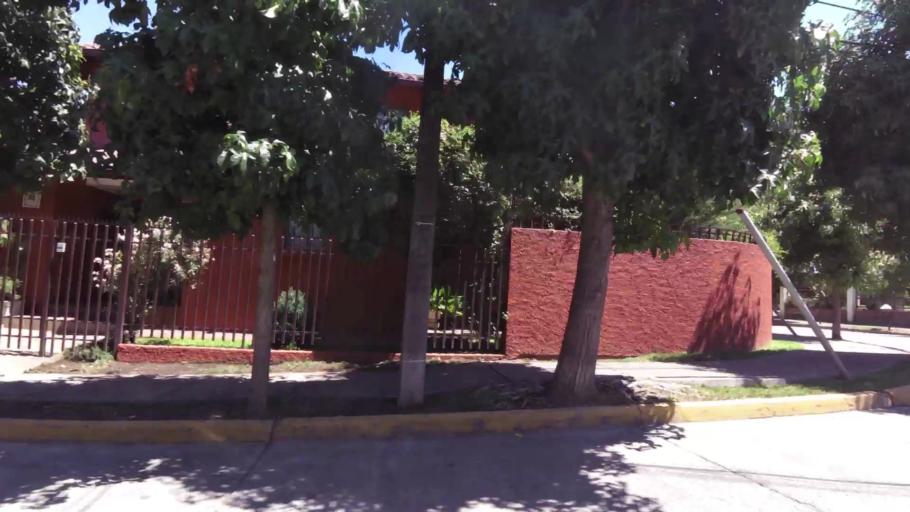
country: CL
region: Maule
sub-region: Provincia de Curico
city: Curico
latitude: -34.9816
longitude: -71.2282
